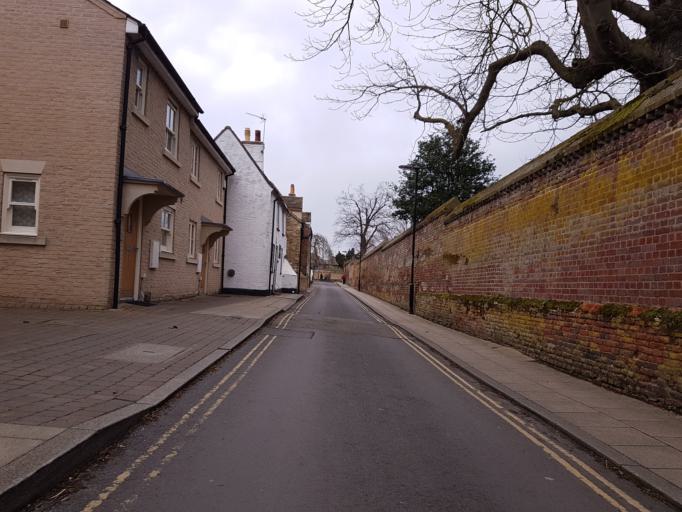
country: GB
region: England
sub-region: Cambridgeshire
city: Ely
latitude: 52.3981
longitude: 0.2604
